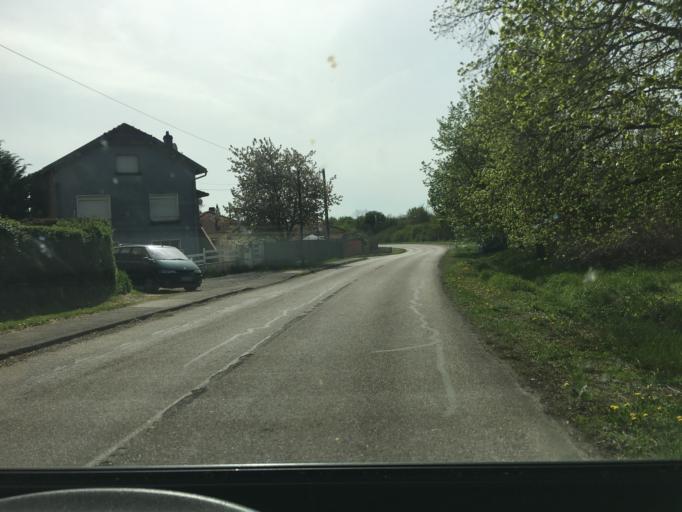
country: FR
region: Lorraine
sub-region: Departement de Meurthe-et-Moselle
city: Chaligny
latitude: 48.6196
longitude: 6.0852
